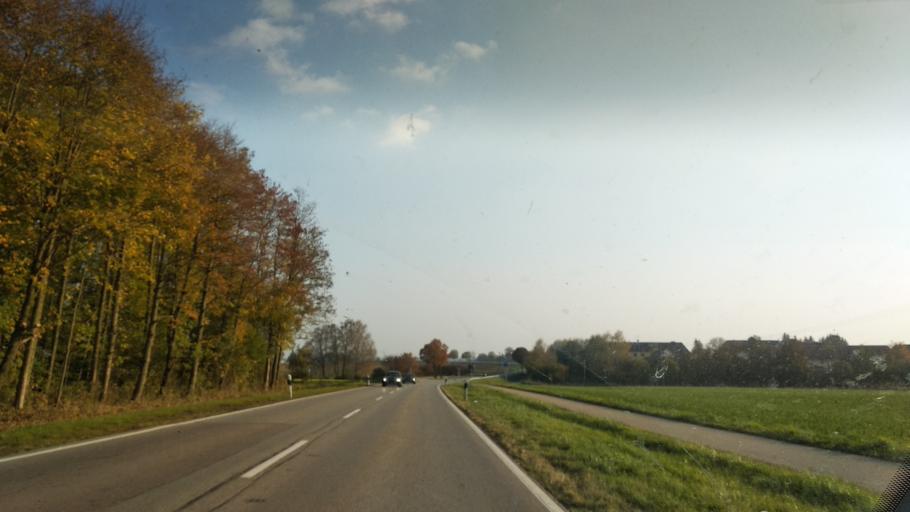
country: DE
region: Bavaria
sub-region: Upper Bavaria
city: Pastetten
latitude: 48.2233
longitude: 11.9452
